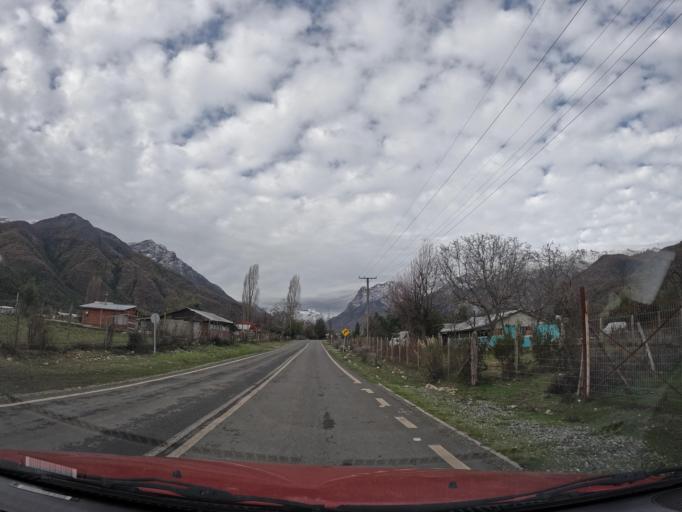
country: CL
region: Maule
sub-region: Provincia de Linares
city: Colbun
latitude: -35.8604
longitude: -71.2626
